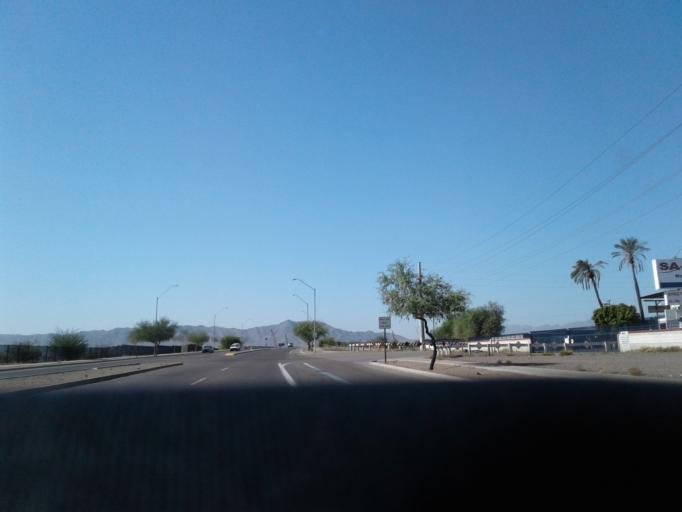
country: US
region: Arizona
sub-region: Maricopa County
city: Laveen
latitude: 33.4146
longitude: -112.1343
